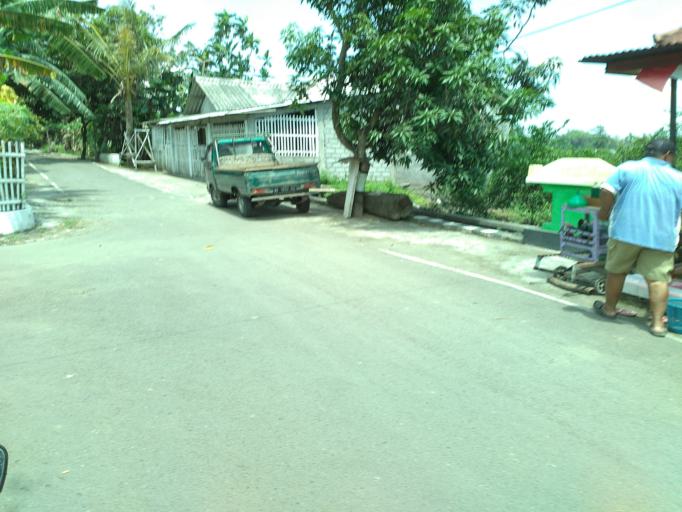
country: ID
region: Central Java
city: Klaten
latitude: -7.7021
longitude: 110.5937
